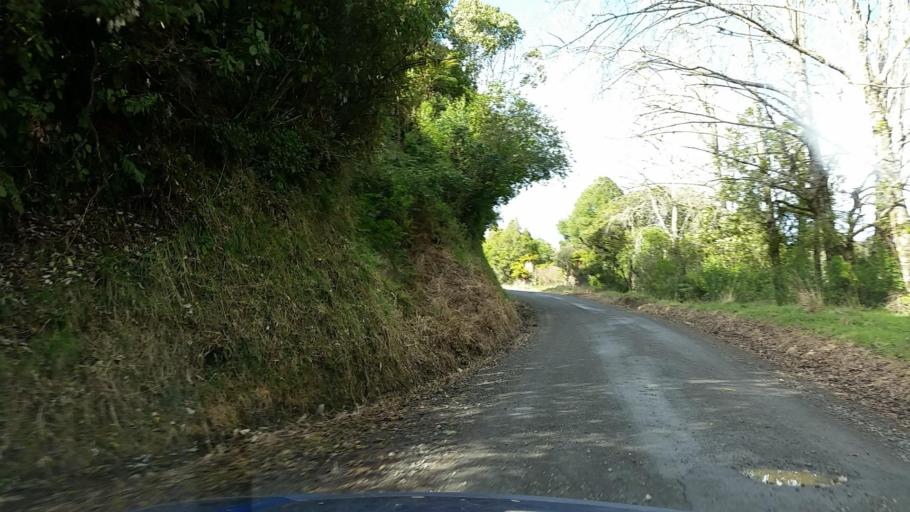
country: NZ
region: Taranaki
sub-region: South Taranaki District
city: Eltham
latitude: -39.2921
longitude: 174.6317
